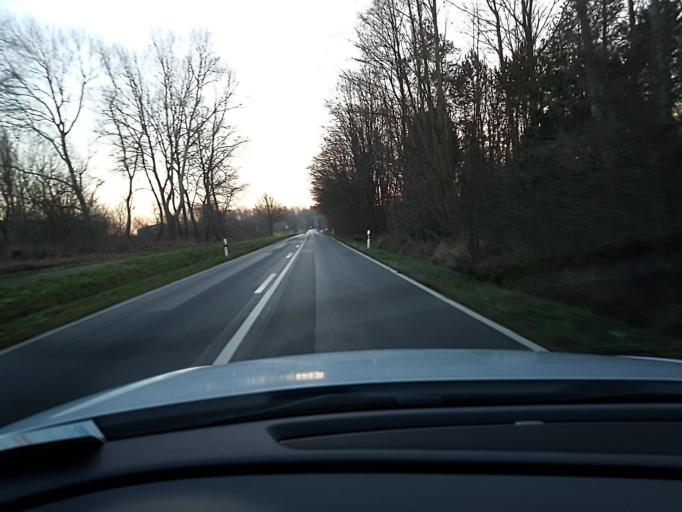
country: DE
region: Mecklenburg-Vorpommern
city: Wiek
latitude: 54.6133
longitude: 13.2839
